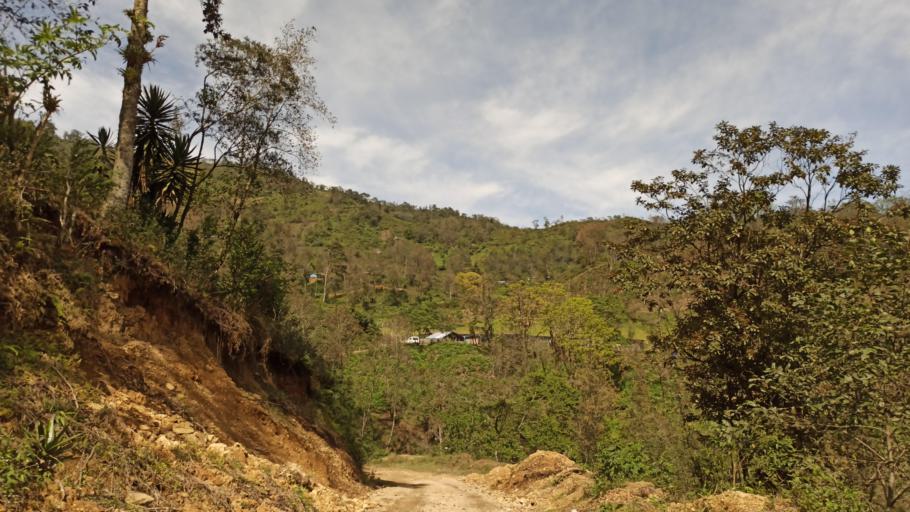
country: MX
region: Veracruz
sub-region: La Perla
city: Metlac Hernandez (Metlac Primero)
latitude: 18.9735
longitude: -97.1054
